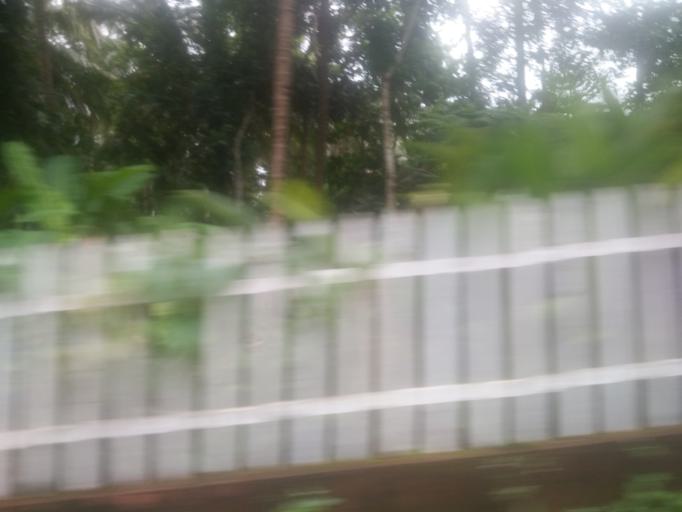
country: IN
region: Goa
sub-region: South Goa
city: Varca
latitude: 15.2195
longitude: 73.9513
